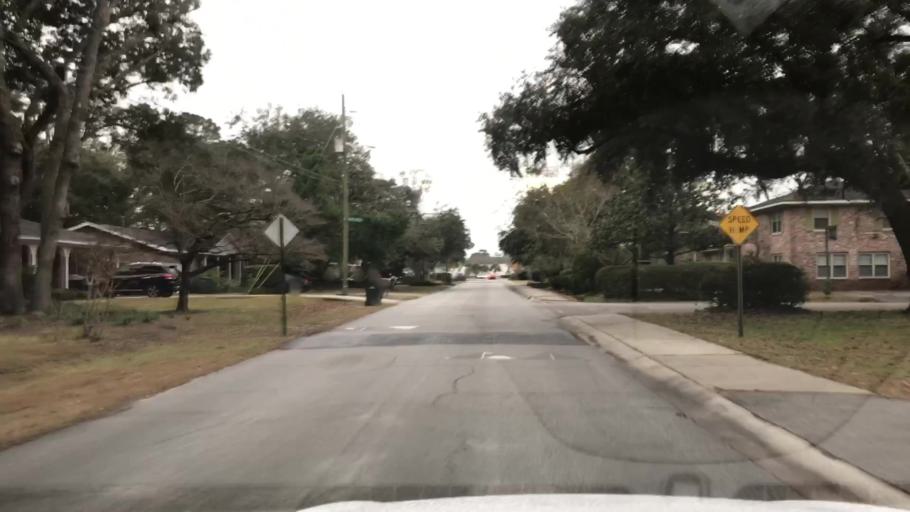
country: US
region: South Carolina
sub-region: Charleston County
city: North Charleston
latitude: 32.8164
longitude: -79.9988
